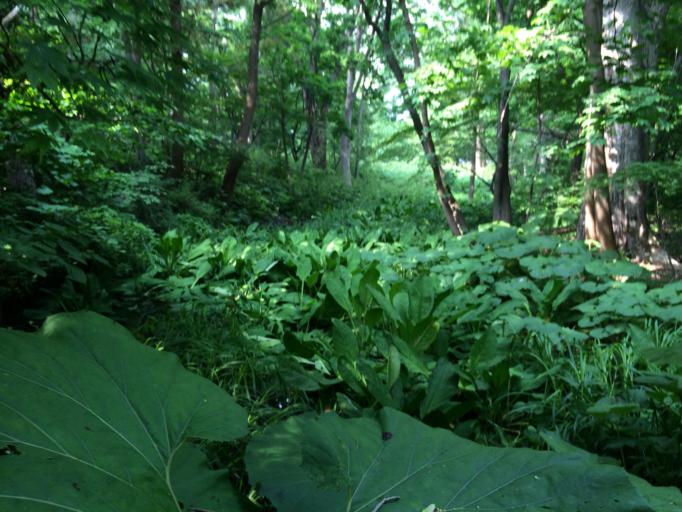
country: JP
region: Hokkaido
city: Sapporo
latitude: 43.0642
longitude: 141.3436
